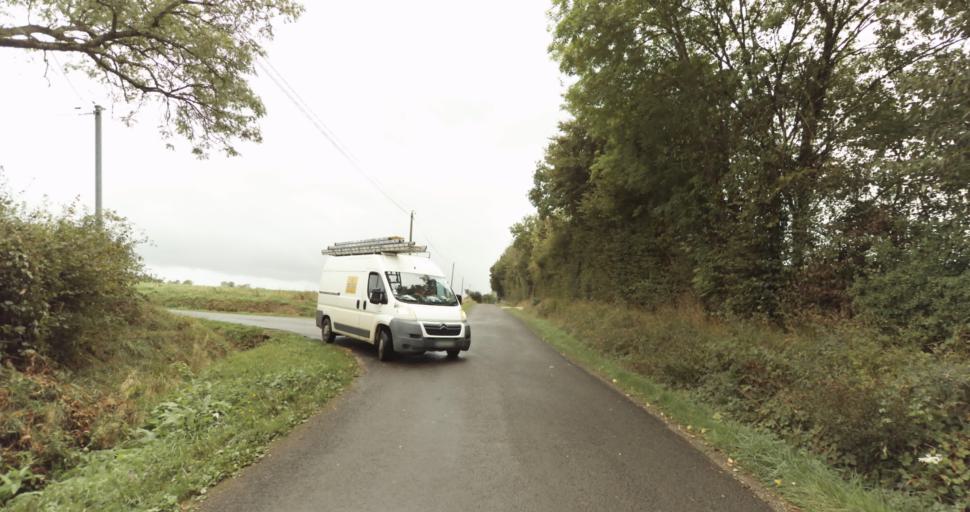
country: FR
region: Lower Normandy
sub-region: Departement de l'Orne
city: Sainte-Gauburge-Sainte-Colombe
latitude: 48.7169
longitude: 0.3792
